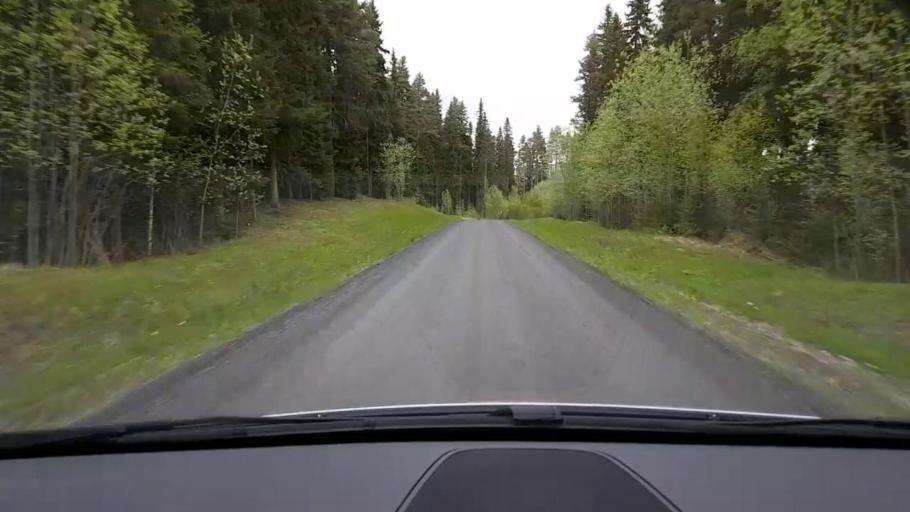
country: SE
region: Jaemtland
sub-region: Krokoms Kommun
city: Krokom
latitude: 63.2959
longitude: 14.3927
